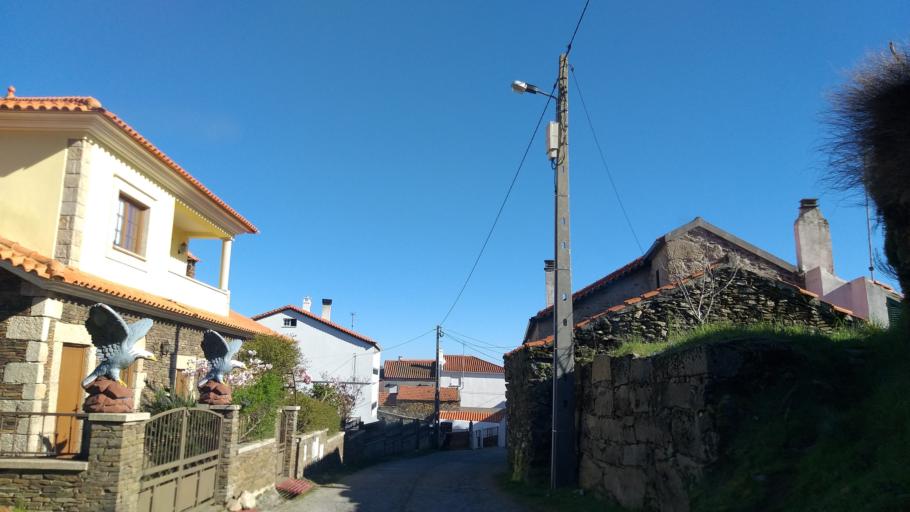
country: PT
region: Guarda
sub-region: Celorico da Beira
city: Celorico da Beira
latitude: 40.5158
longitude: -7.3952
